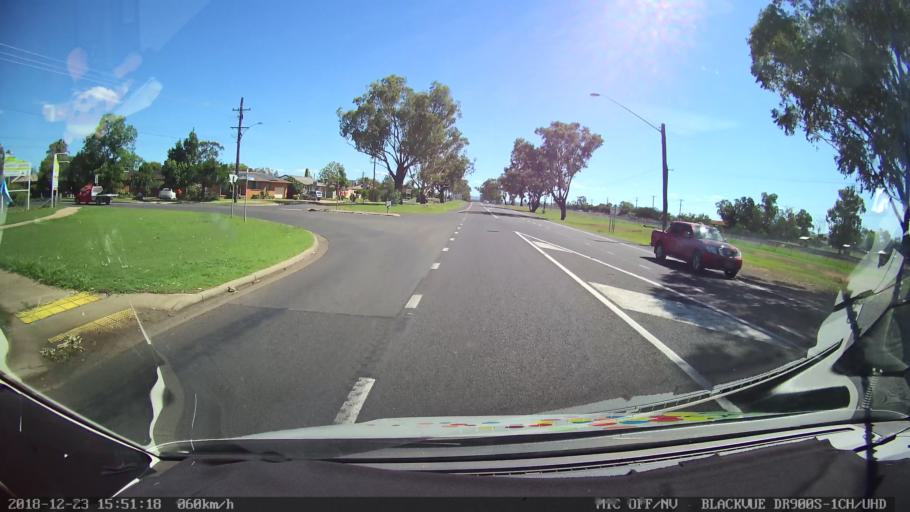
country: AU
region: New South Wales
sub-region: Tamworth Municipality
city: South Tamworth
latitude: -31.1117
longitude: 150.8967
